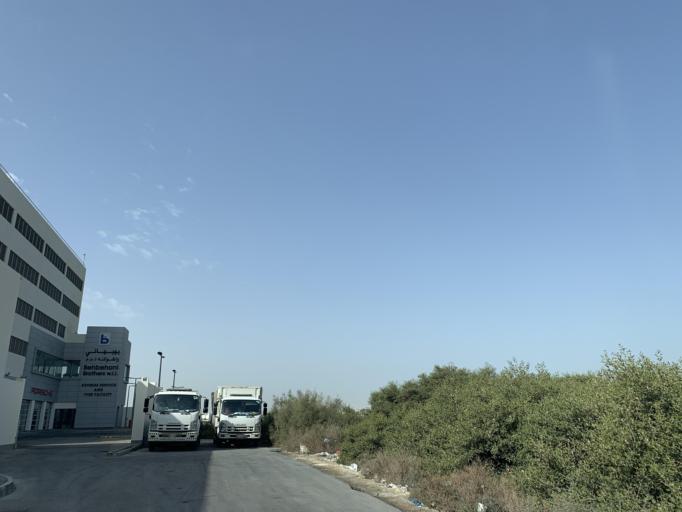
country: BH
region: Northern
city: Sitrah
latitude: 26.1538
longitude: 50.6080
